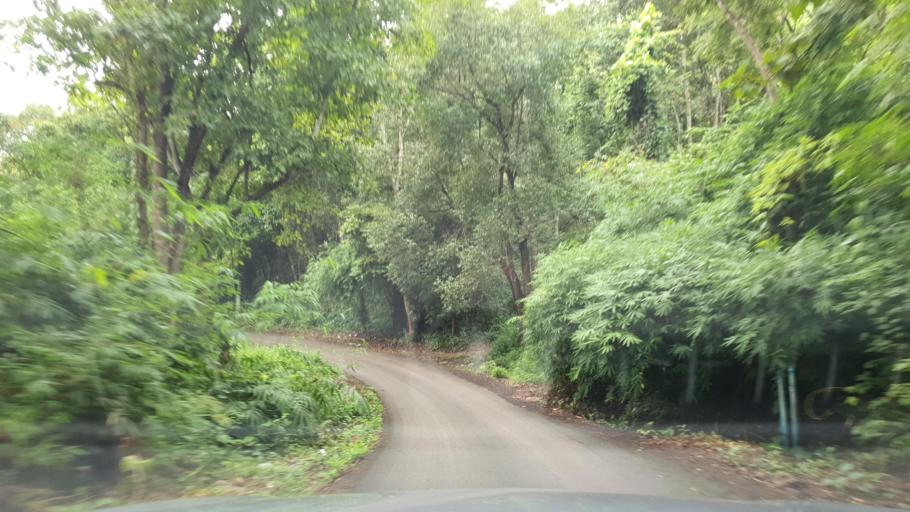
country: TH
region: Chiang Mai
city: Mae Taeng
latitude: 19.2067
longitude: 98.9326
